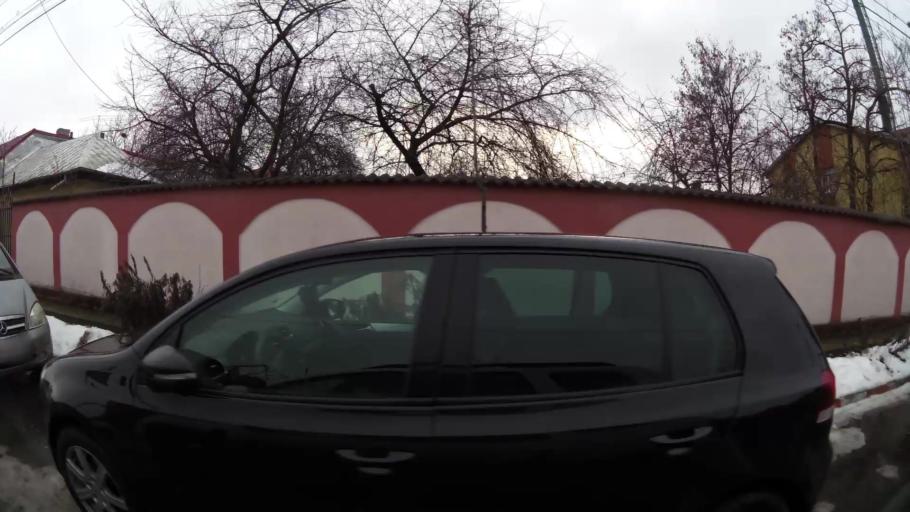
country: RO
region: Ilfov
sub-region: Voluntari City
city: Voluntari
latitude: 44.4811
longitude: 26.1741
